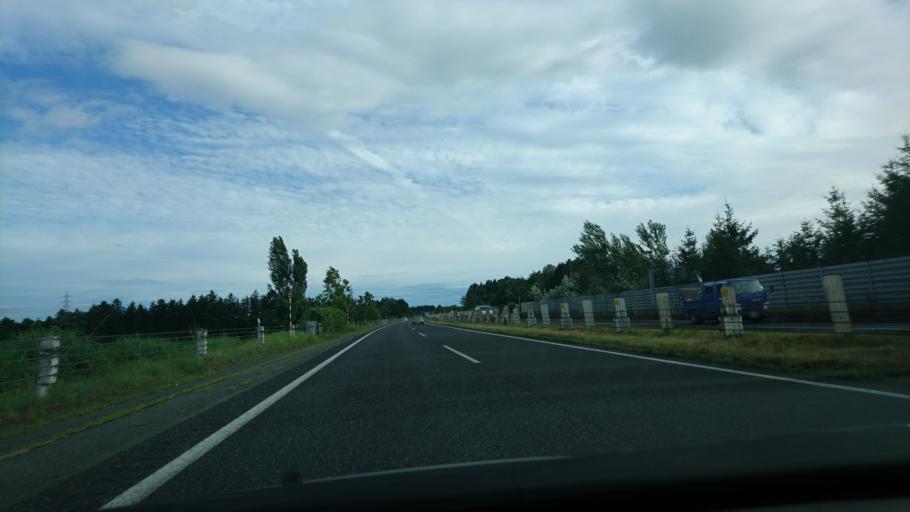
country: JP
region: Iwate
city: Hanamaki
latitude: 39.3398
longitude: 141.0916
